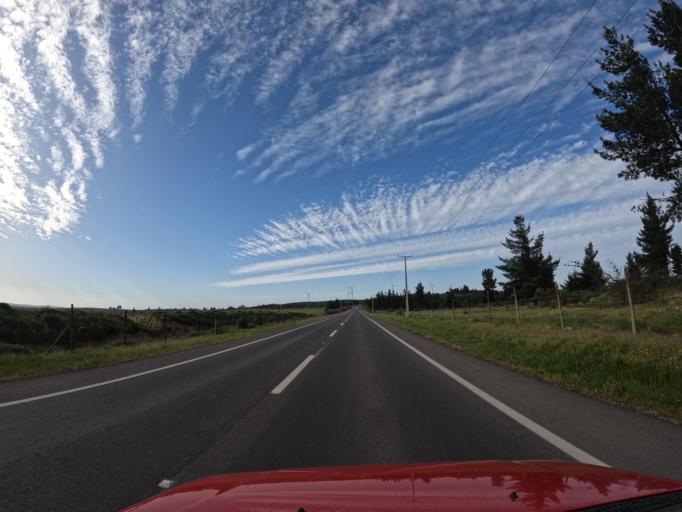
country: CL
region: Valparaiso
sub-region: San Antonio Province
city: San Antonio
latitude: -34.0638
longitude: -71.6263
